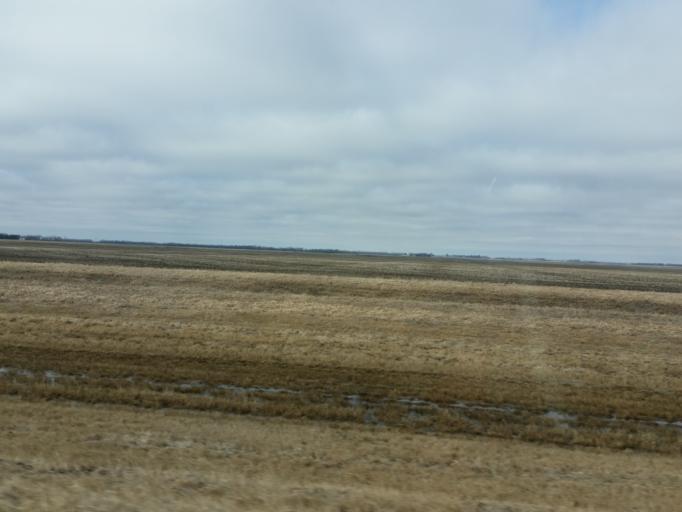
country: US
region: North Dakota
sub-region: Cass County
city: Casselton
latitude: 46.9663
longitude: -97.2194
